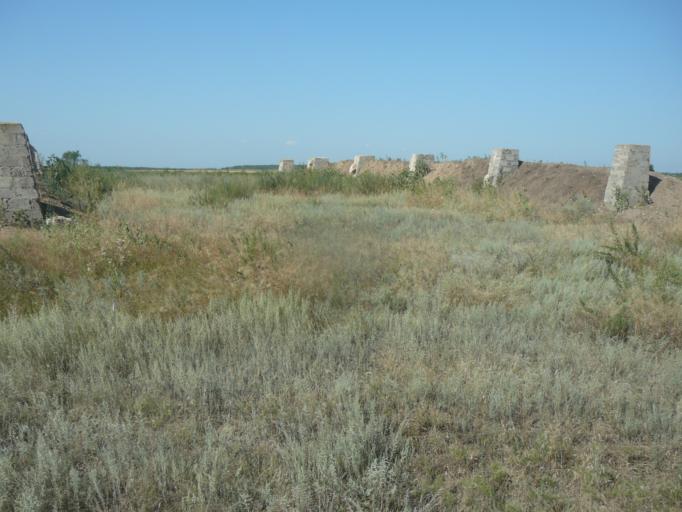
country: RU
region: Saratov
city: Krasnyy Yar
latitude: 51.5677
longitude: 46.5296
